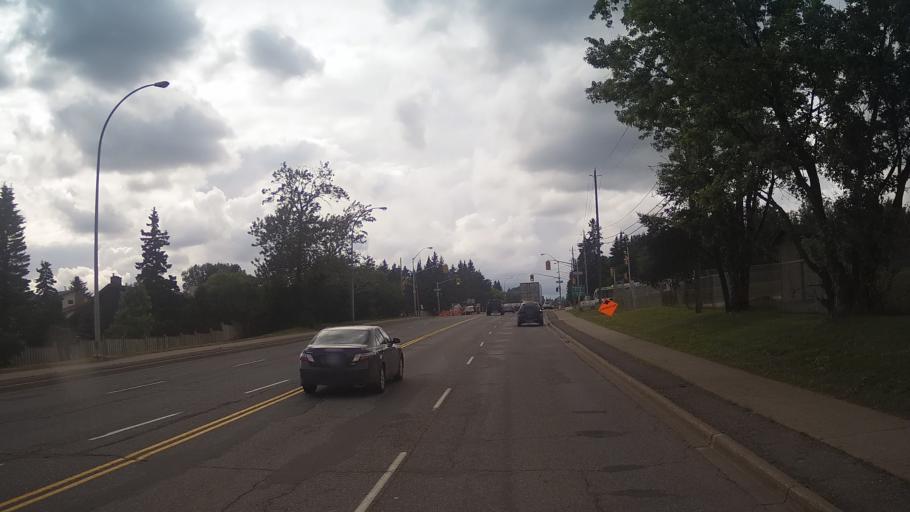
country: CA
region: Ontario
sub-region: Thunder Bay District
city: Thunder Bay
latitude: 48.4532
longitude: -89.2581
